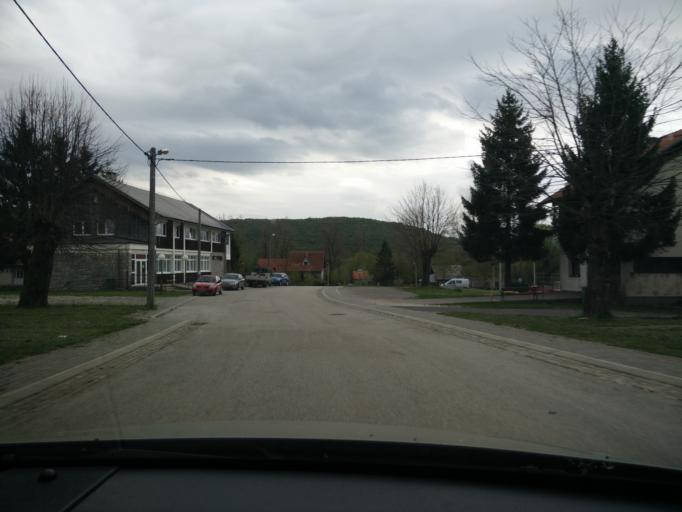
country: HR
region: Zadarska
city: Obrovac
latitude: 44.3916
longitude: 15.6865
